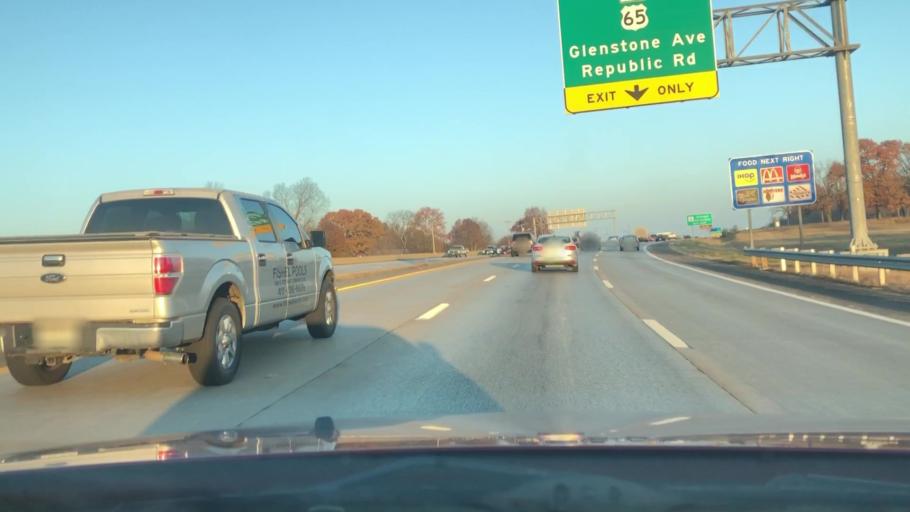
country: US
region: Missouri
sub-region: Greene County
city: Springfield
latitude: 37.1326
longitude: -93.2442
